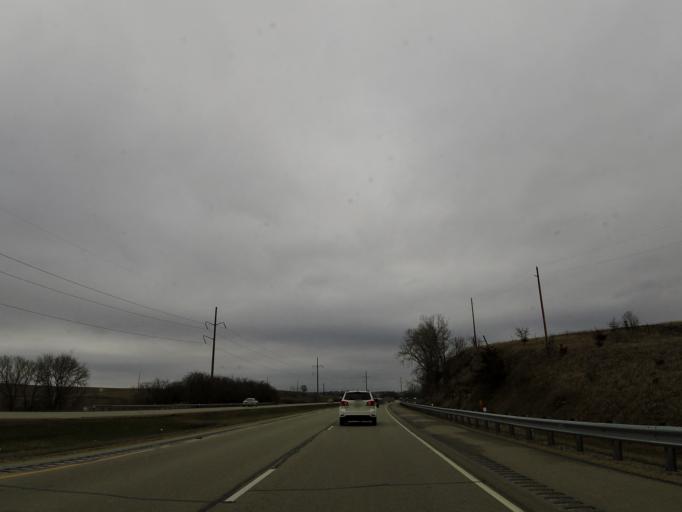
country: US
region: Minnesota
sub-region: Olmsted County
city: Rochester
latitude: 44.0383
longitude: -92.5485
